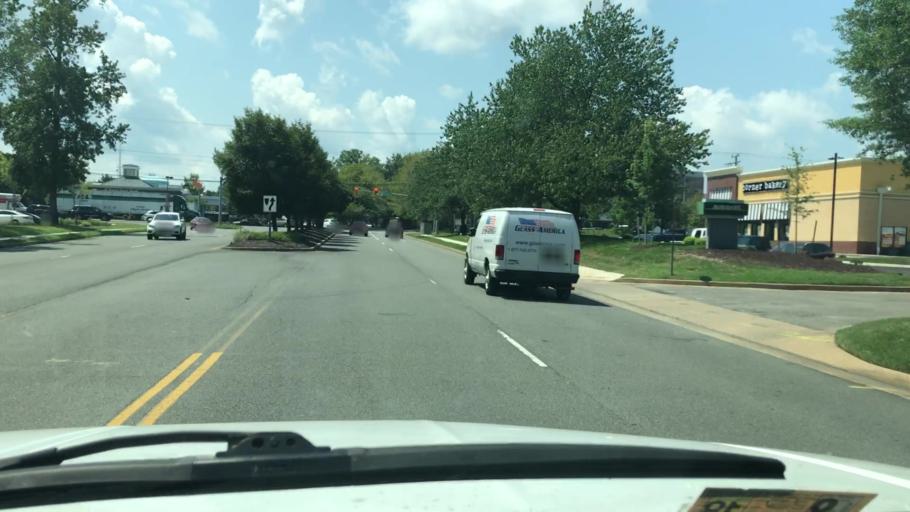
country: US
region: Virginia
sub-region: Henrico County
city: Short Pump
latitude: 37.6484
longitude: -77.5863
